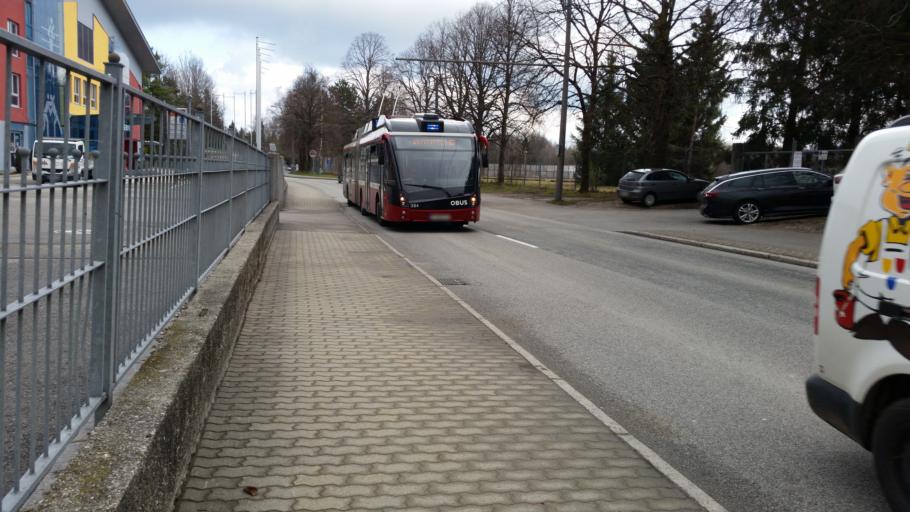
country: DE
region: Bavaria
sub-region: Upper Bavaria
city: Ainring
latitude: 47.7950
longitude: 12.9821
